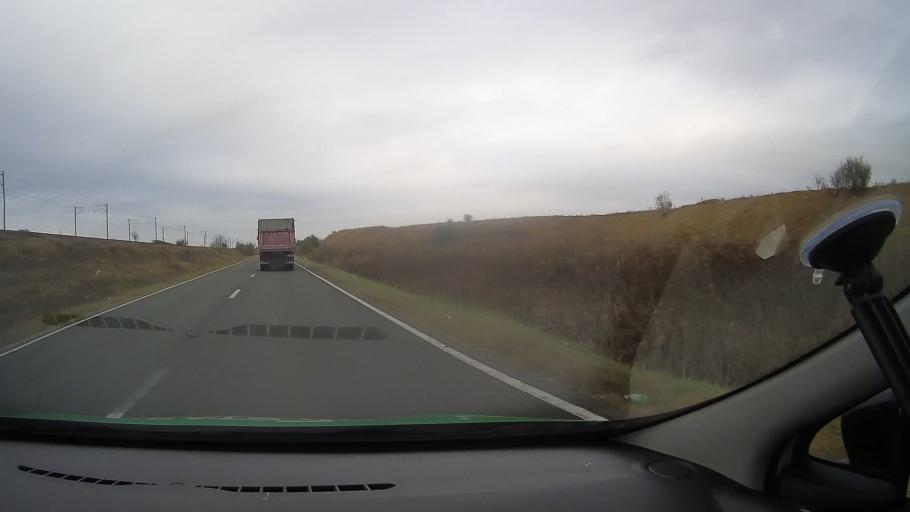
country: RO
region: Constanta
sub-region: Comuna Poarta Alba
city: Poarta Alba
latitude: 44.2232
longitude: 28.3857
